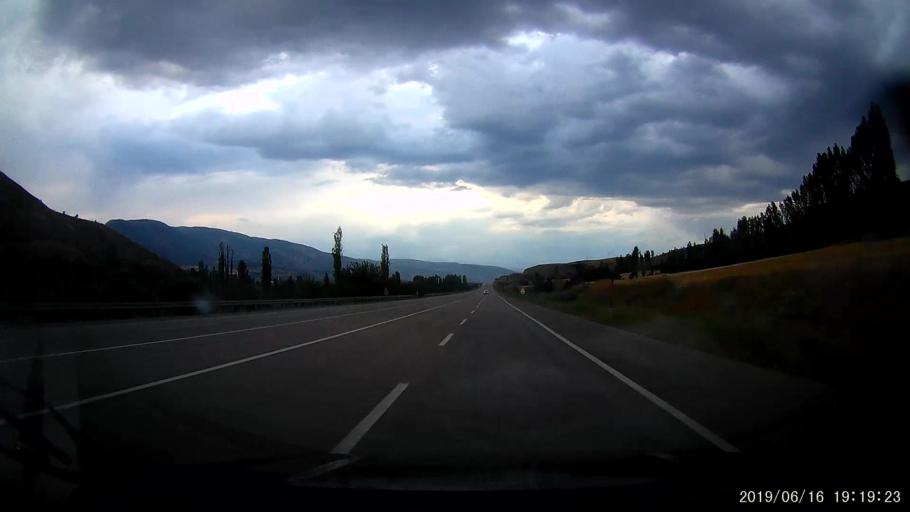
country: TR
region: Sivas
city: Akincilar
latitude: 40.0944
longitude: 38.4307
